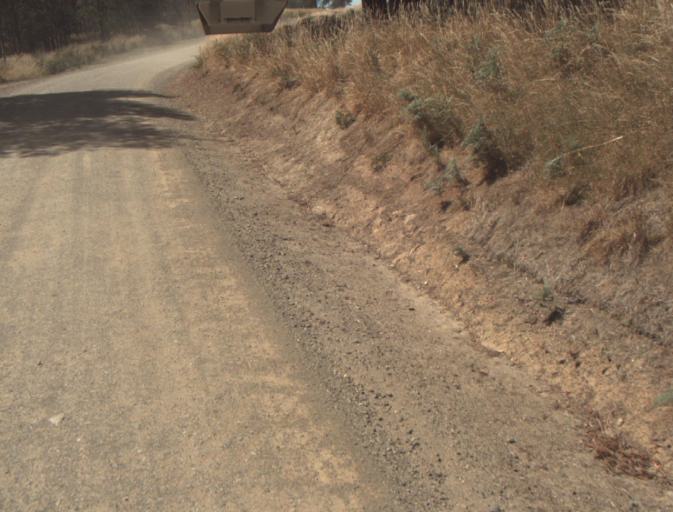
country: AU
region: Tasmania
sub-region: Dorset
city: Scottsdale
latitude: -41.3332
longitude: 147.4337
